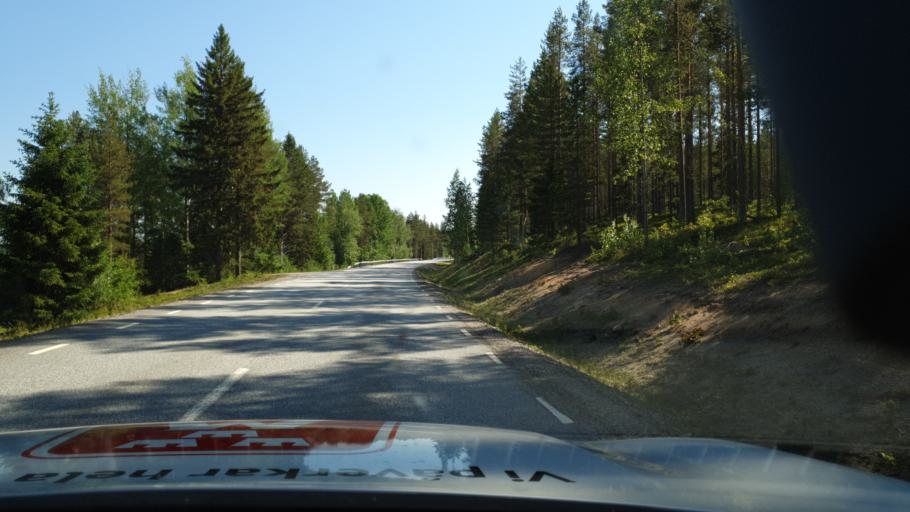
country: SE
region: Vaesterbotten
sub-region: Umea Kommun
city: Ersmark
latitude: 64.2728
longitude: 20.2291
